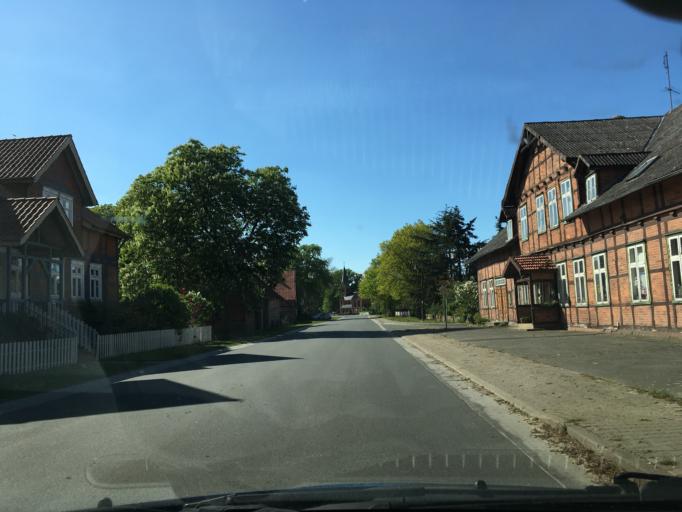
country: DE
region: Lower Saxony
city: Gartow
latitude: 53.0184
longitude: 11.5329
